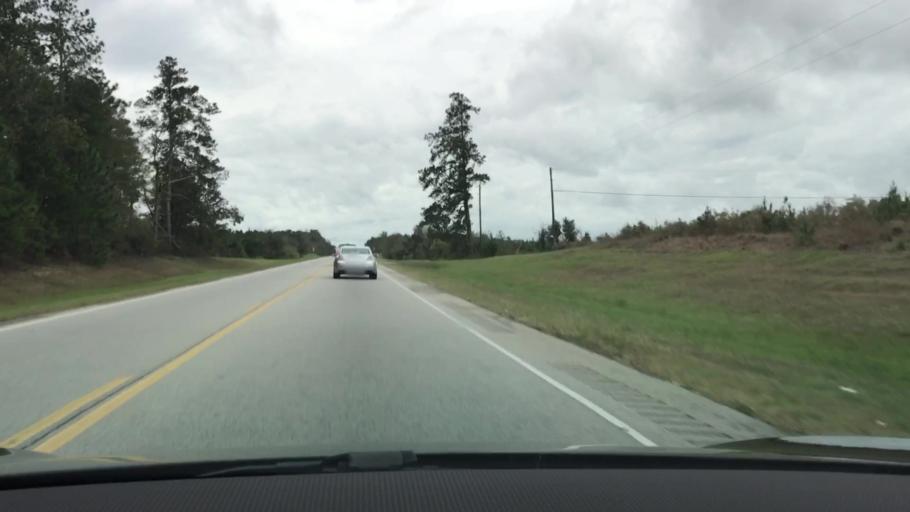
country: US
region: Georgia
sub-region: Jefferson County
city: Wadley
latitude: 32.9084
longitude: -82.3992
